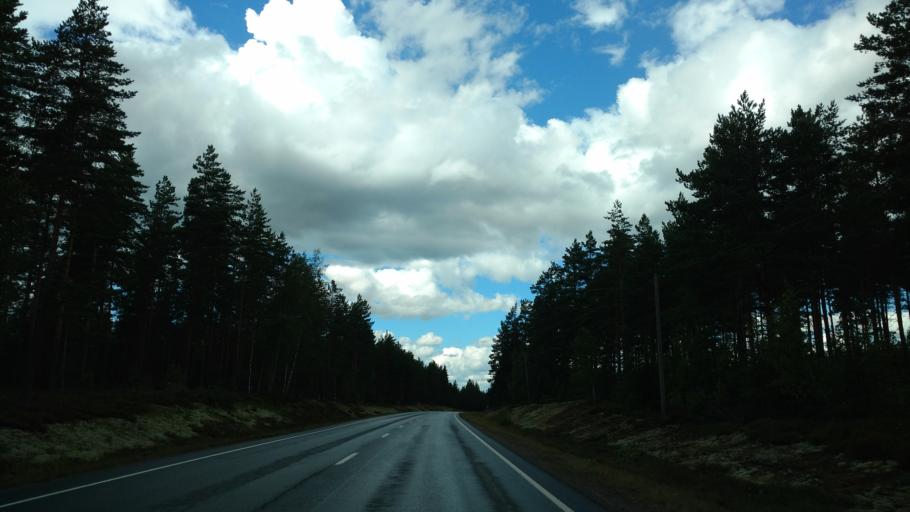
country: FI
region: Varsinais-Suomi
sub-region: Salo
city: Muurla
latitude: 60.2946
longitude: 23.3341
